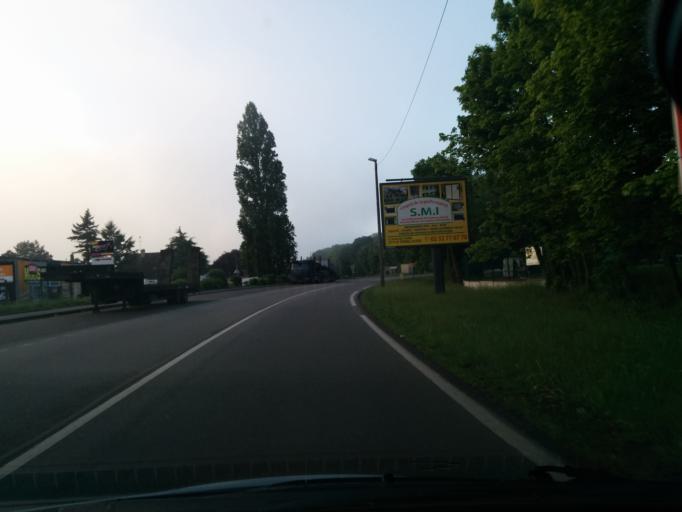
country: FR
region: Haute-Normandie
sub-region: Departement de l'Eure
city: Vernon
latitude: 49.0820
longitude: 1.5036
